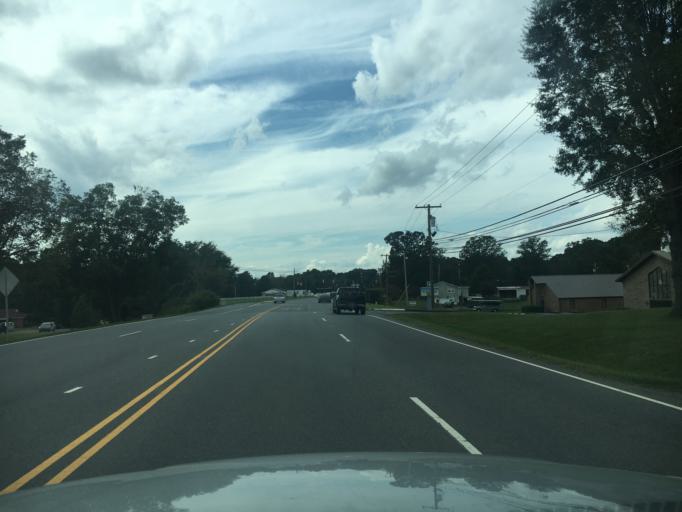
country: US
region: North Carolina
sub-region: Gaston County
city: Dallas
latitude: 35.3155
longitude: -81.1978
